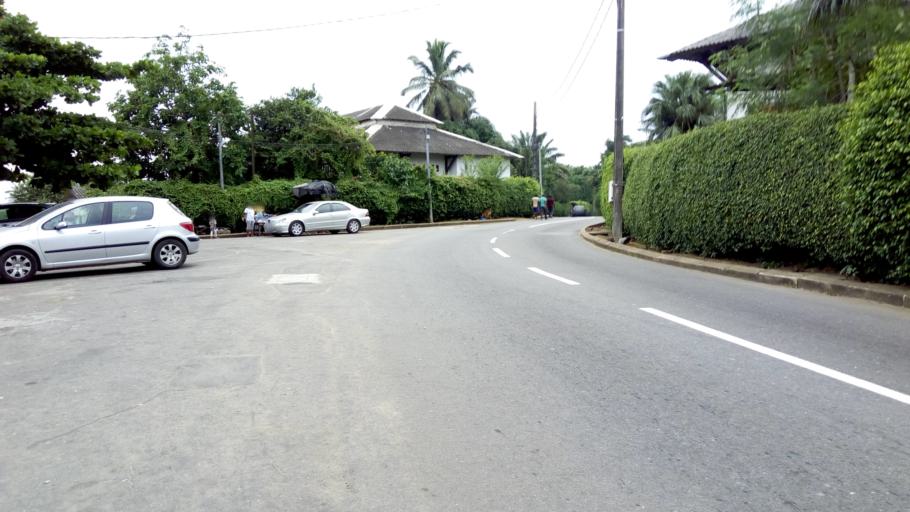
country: CI
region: Lagunes
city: Abidjan
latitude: 5.3227
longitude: -4.0241
